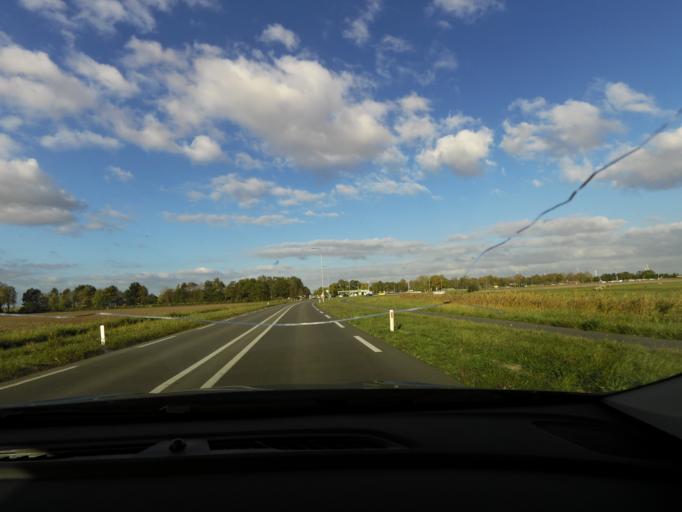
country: NL
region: North Brabant
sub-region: Gemeente Steenbergen
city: Dinteloord
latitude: 51.6266
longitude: 4.3619
